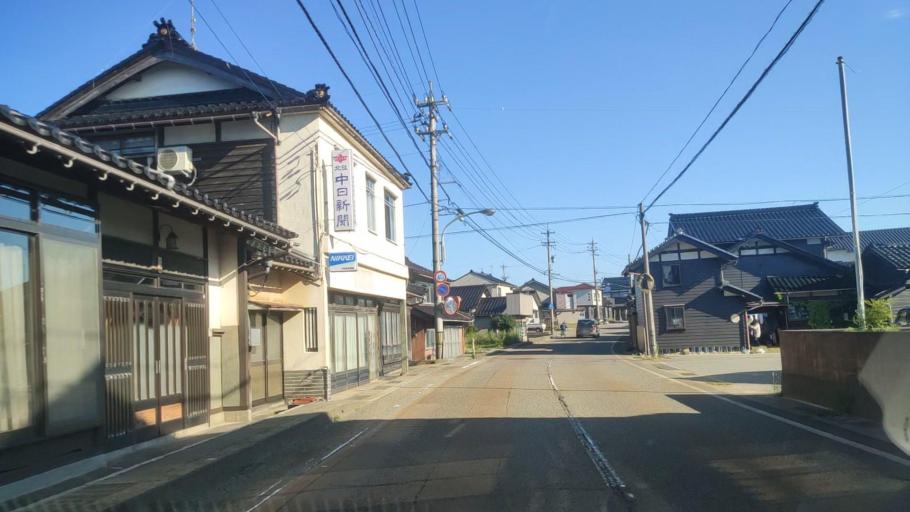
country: JP
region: Ishikawa
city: Hakui
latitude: 36.8231
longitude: 136.7562
